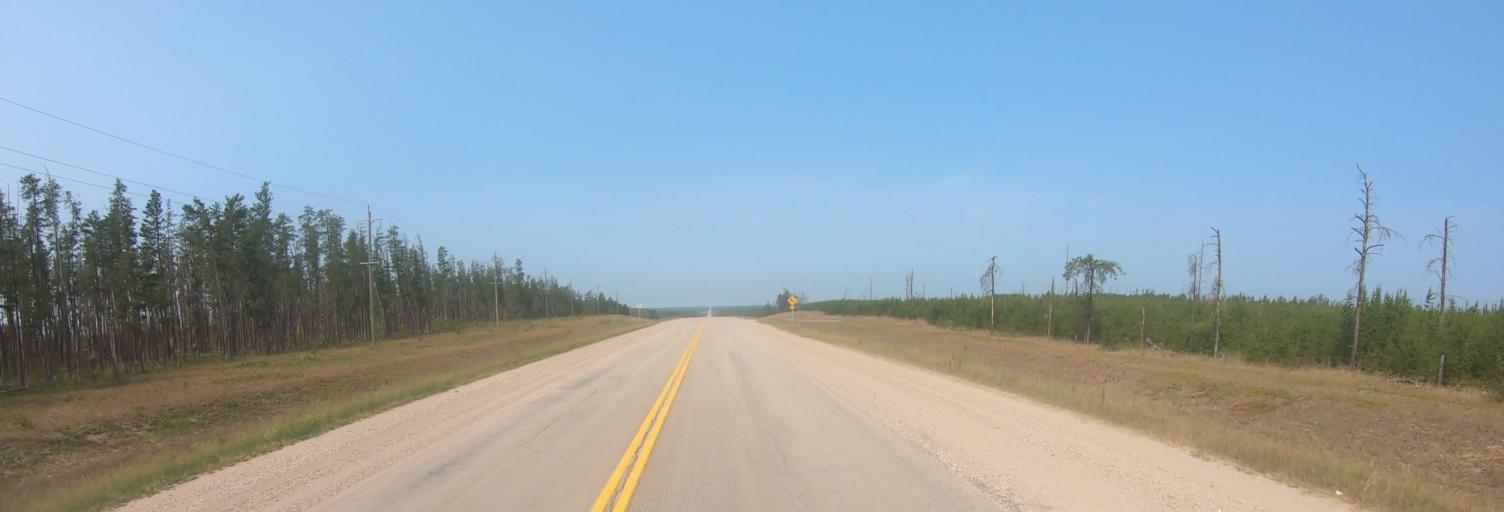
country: US
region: Minnesota
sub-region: Roseau County
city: Roseau
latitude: 49.0896
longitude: -95.8946
